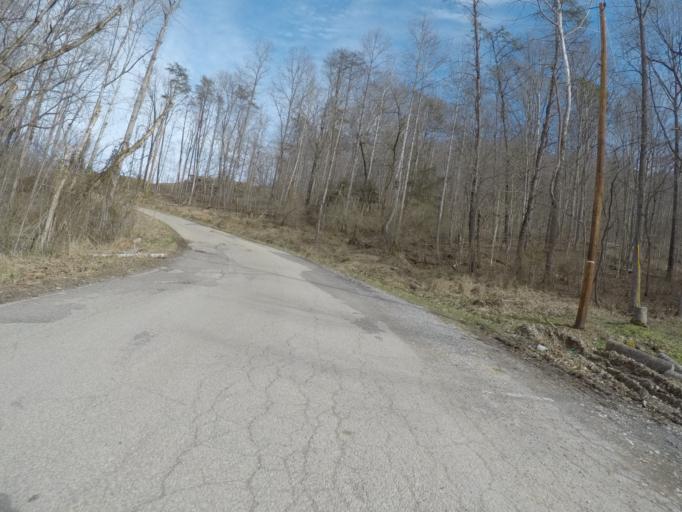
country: US
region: West Virginia
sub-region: Wayne County
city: Lavalette
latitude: 38.3368
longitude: -82.5004
